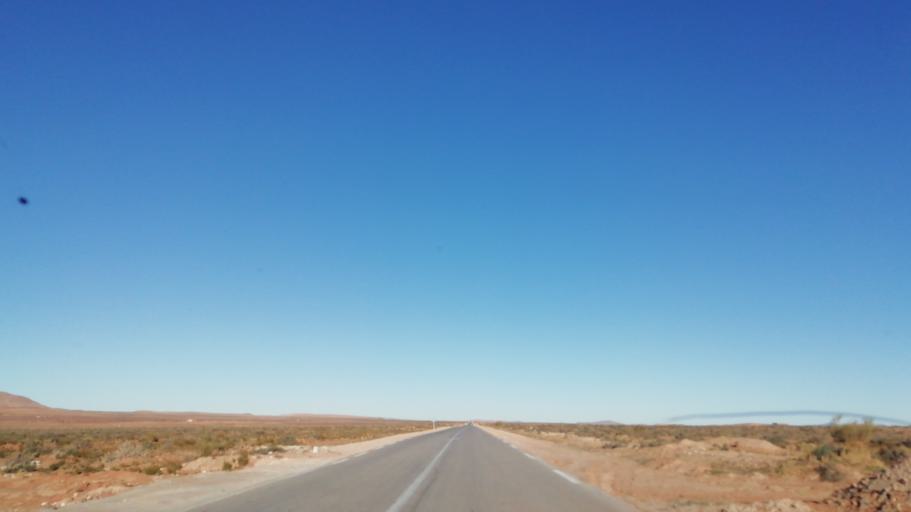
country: DZ
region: El Bayadh
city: El Abiodh Sidi Cheikh
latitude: 33.1136
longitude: 0.2631
